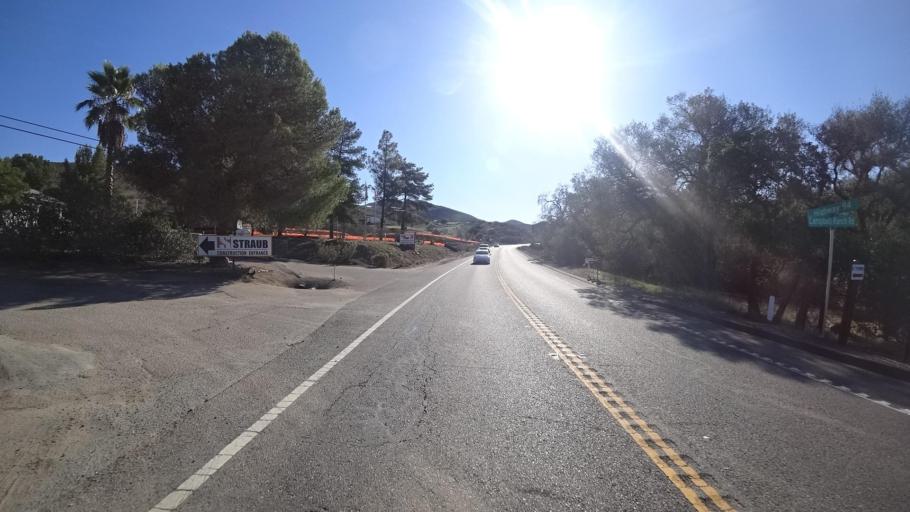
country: US
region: California
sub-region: San Diego County
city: Jamul
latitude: 32.6425
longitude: -116.7754
